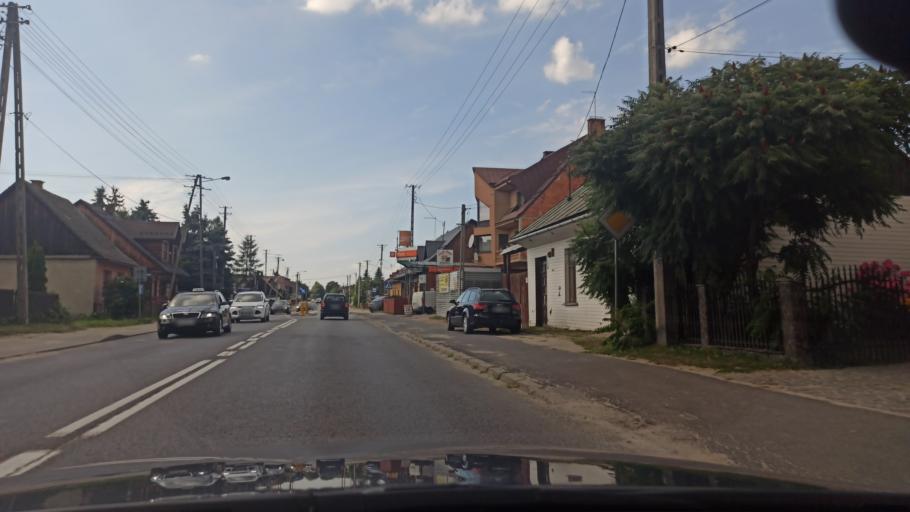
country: PL
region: Lesser Poland Voivodeship
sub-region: Powiat nowotarski
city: Waksmund
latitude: 49.4820
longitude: 20.0735
